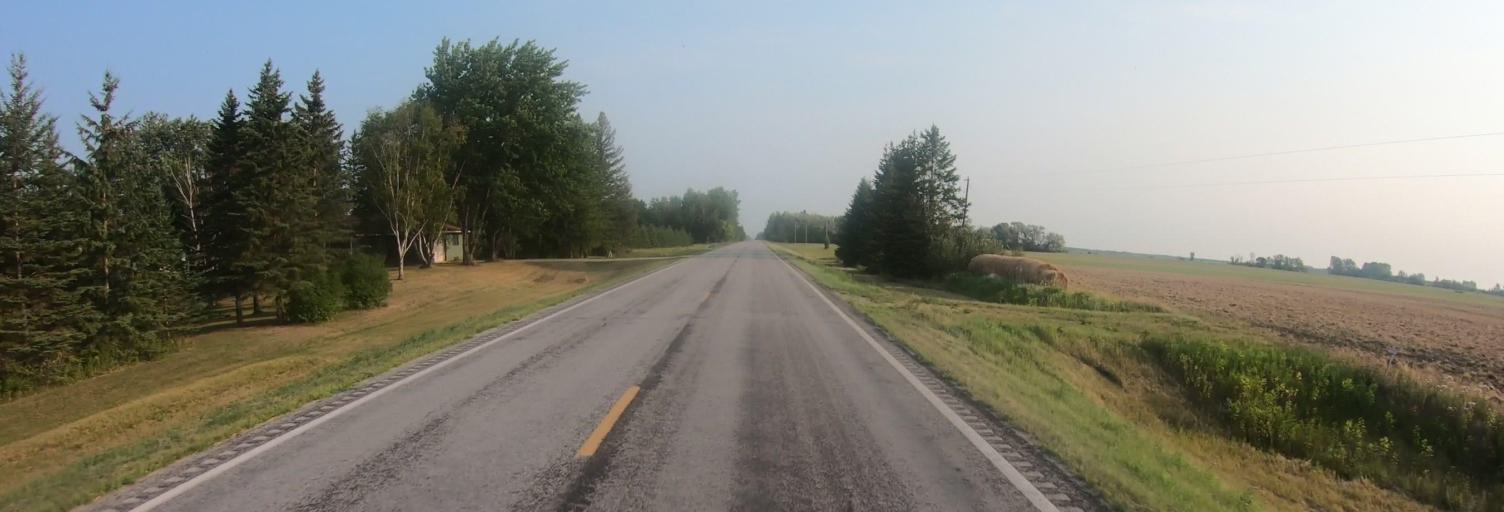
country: US
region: Minnesota
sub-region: Roseau County
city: Warroad
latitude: 48.7770
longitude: -95.3305
